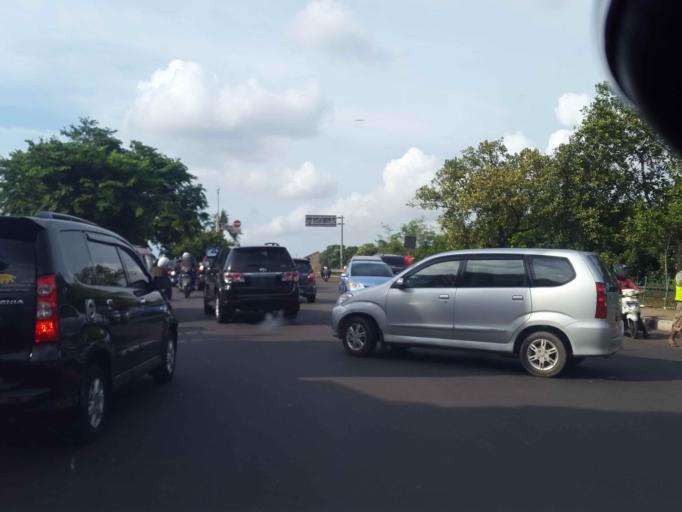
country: ID
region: Jakarta Raya
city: Jakarta
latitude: -6.2583
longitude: 106.9101
